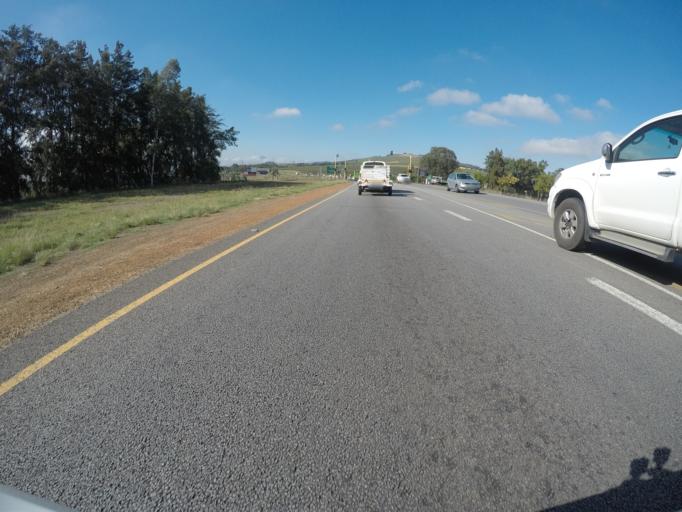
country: ZA
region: Western Cape
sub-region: Cape Winelands District Municipality
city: Stellenbosch
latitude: -33.8740
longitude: 18.8140
